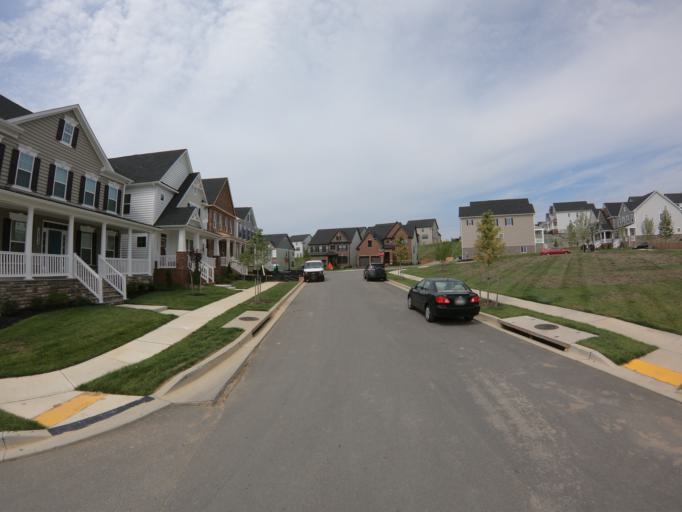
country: US
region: Maryland
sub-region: Montgomery County
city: Clarksburg
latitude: 39.2176
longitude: -77.2876
